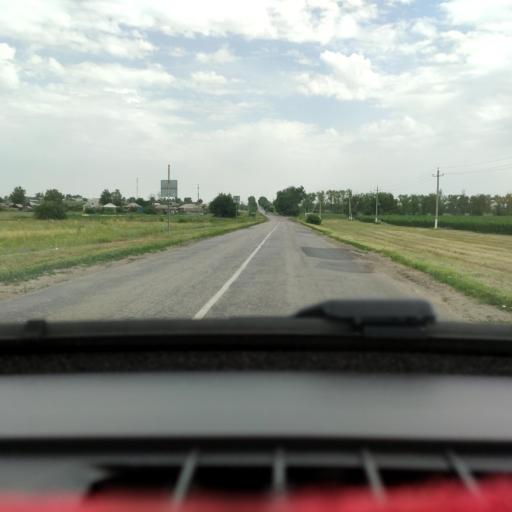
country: RU
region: Voronezj
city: Davydovka
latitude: 51.2372
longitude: 39.5383
